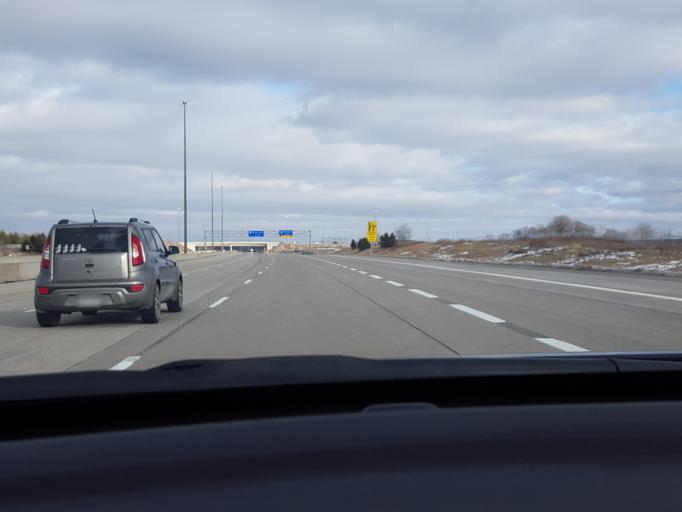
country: CA
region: Ontario
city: Markham
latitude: 43.8596
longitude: -79.2663
